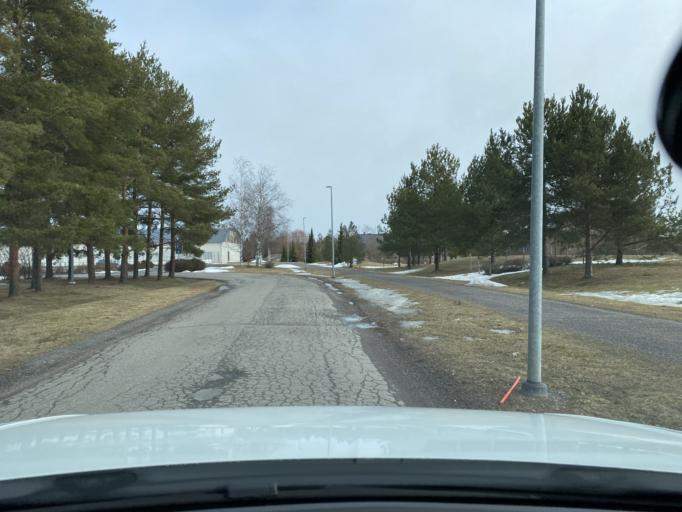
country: FI
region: Satakunta
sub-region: Pori
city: Huittinen
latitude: 61.1825
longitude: 22.6924
